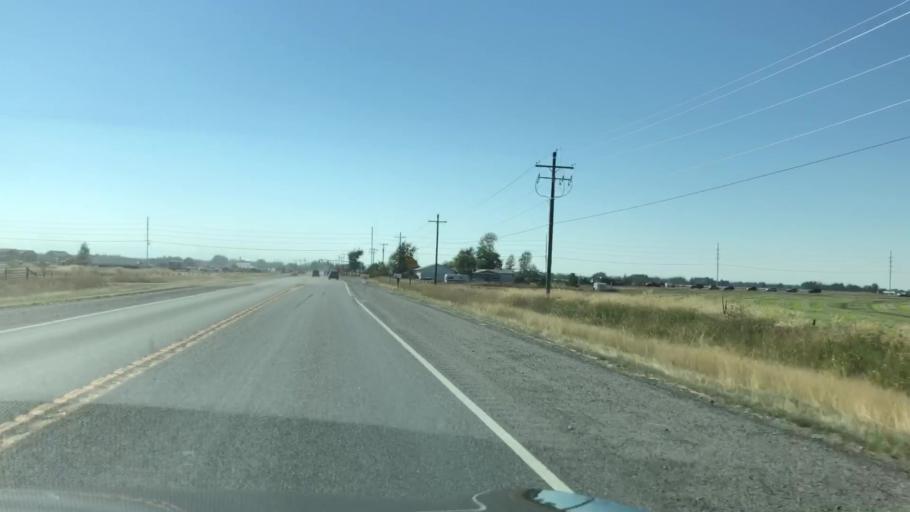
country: US
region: Montana
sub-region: Gallatin County
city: Belgrade
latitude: 45.7292
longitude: -111.1806
